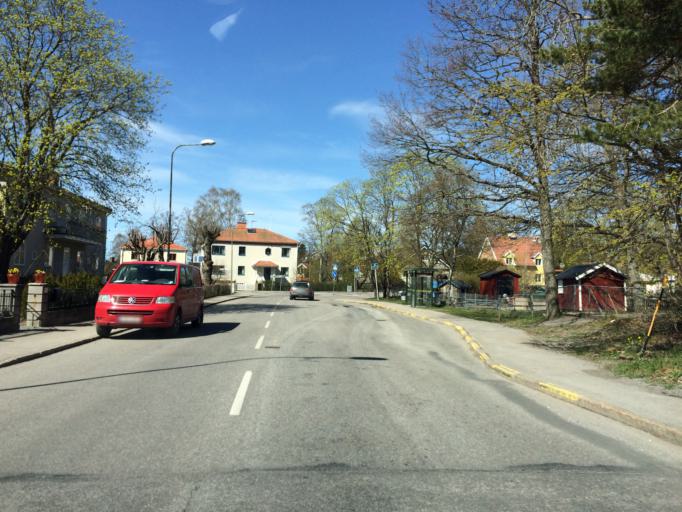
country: SE
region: Stockholm
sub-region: Huddinge Kommun
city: Segeltorp
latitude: 59.2749
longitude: 17.9616
